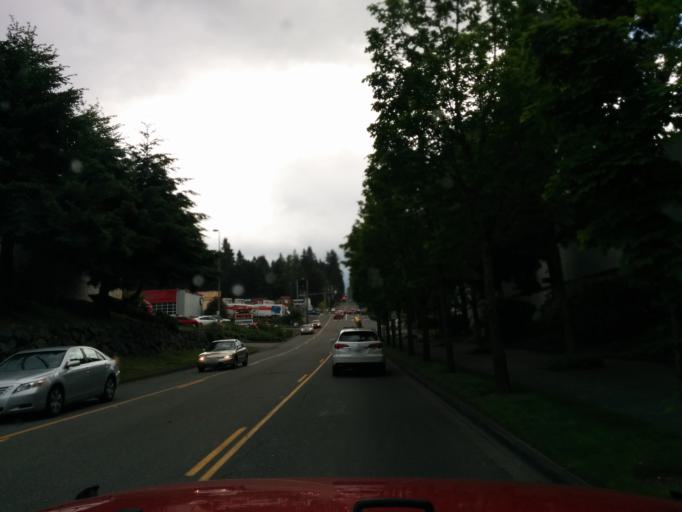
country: US
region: Washington
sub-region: King County
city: Kirkland
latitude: 47.6810
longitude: -122.1807
